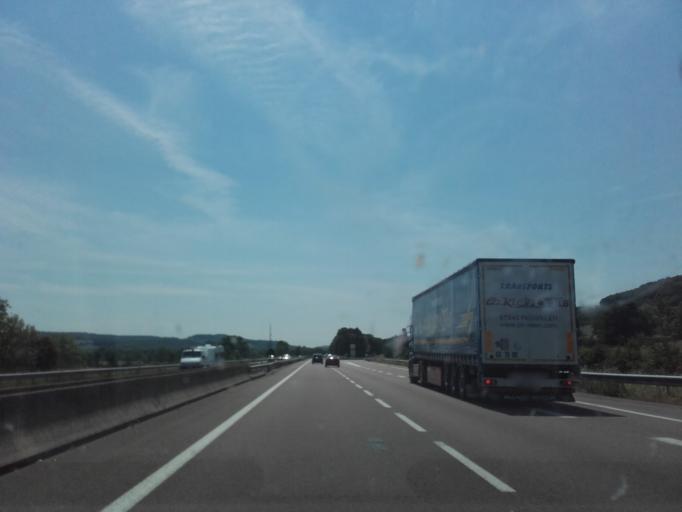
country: FR
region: Bourgogne
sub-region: Departement de la Cote-d'Or
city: Pouilly-en-Auxois
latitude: 47.3202
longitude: 4.4918
